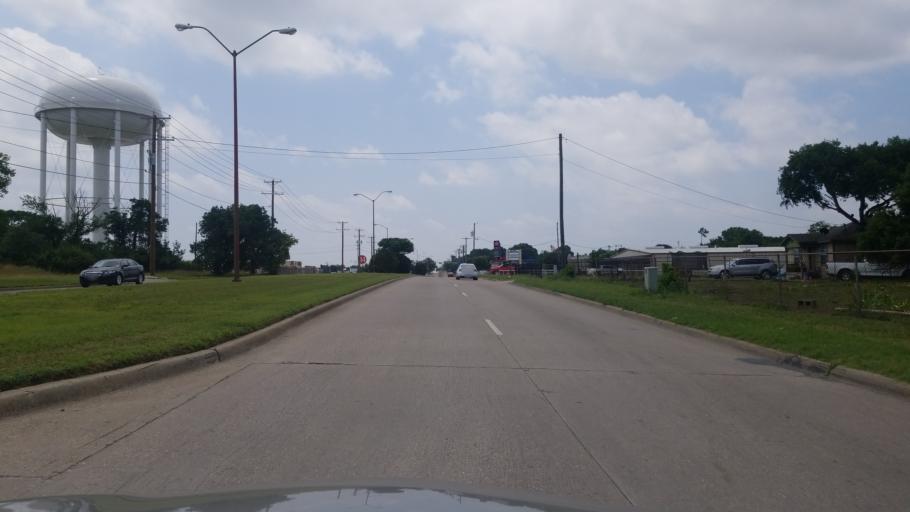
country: US
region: Texas
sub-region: Dallas County
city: Duncanville
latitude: 32.6774
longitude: -96.9086
